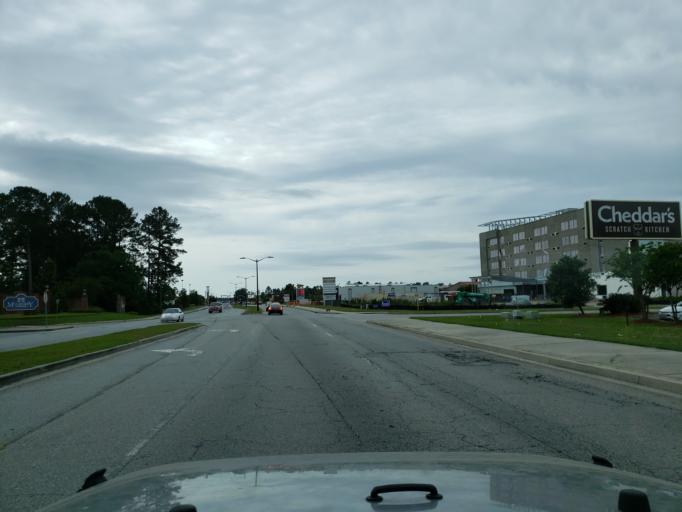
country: US
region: Georgia
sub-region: Chatham County
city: Pooler
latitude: 32.1465
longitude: -81.2476
